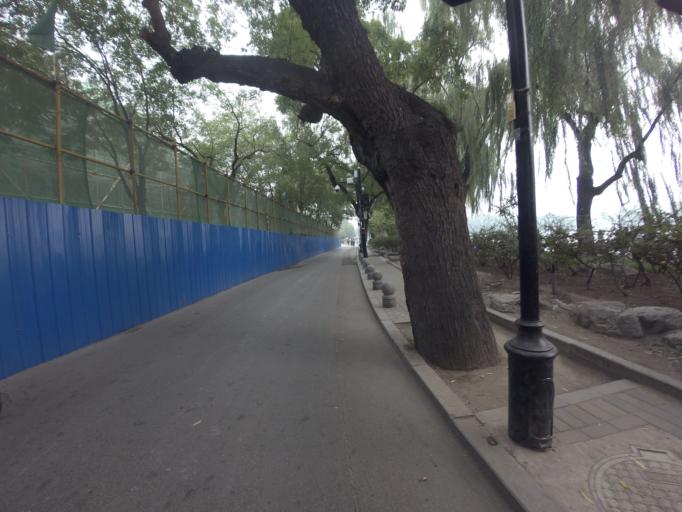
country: CN
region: Beijing
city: Jingshan
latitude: 39.9366
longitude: 116.3887
